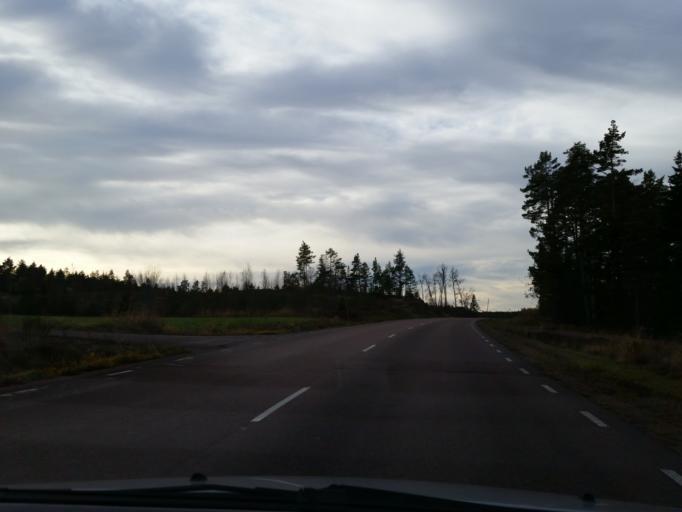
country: AX
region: Alands landsbygd
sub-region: Saltvik
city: Saltvik
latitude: 60.2617
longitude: 20.0542
